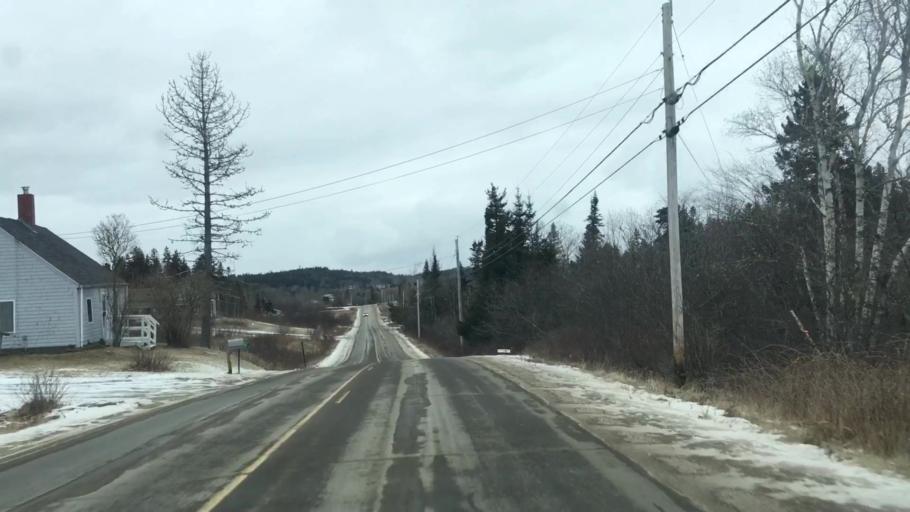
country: US
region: Maine
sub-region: Washington County
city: Machiasport
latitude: 44.7073
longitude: -67.4026
